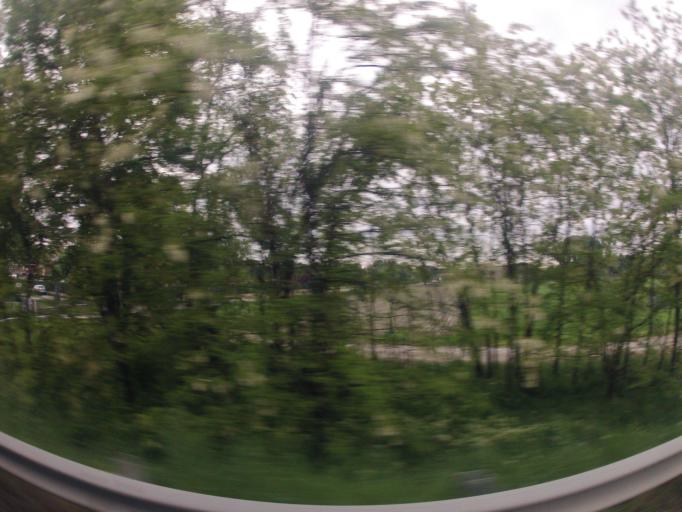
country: IT
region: Piedmont
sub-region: Provincia di Torino
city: La Loggia
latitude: 44.9644
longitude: 7.6765
